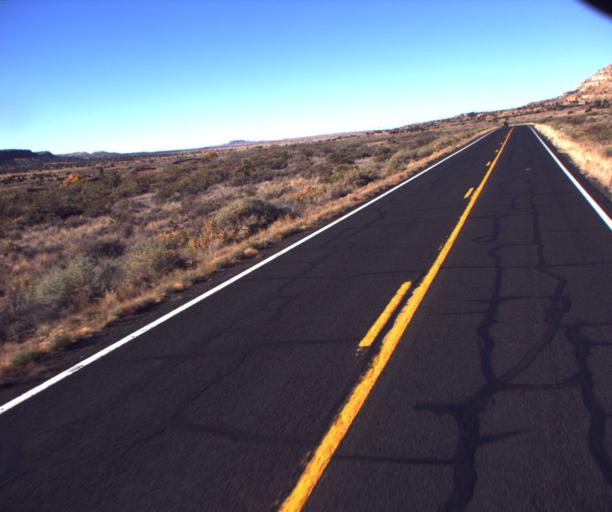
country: US
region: Arizona
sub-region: Navajo County
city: First Mesa
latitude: 35.8407
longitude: -110.2526
